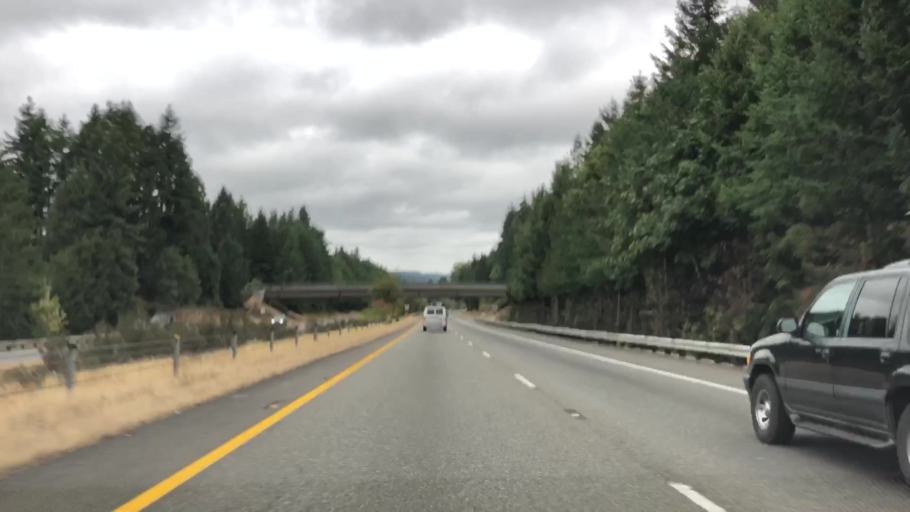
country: US
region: Washington
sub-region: Pierce County
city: Purdy
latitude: 47.3968
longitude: -122.6209
